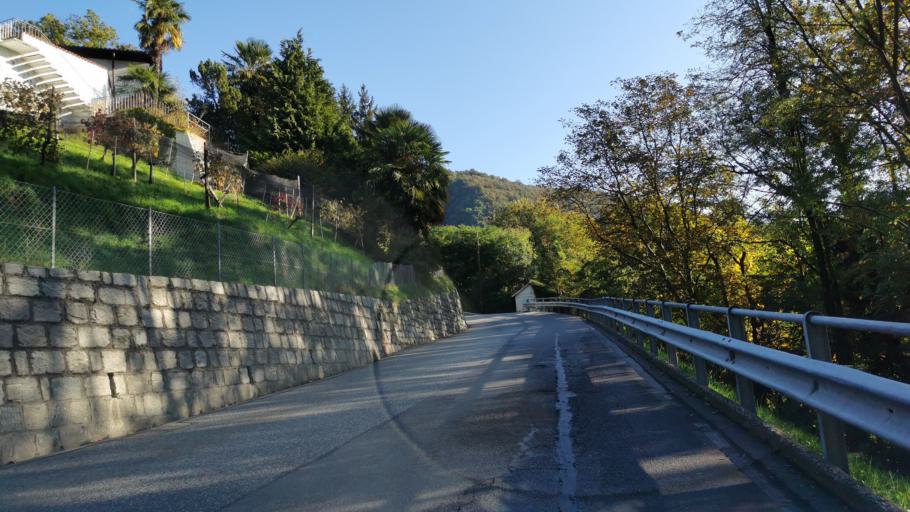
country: CH
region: Ticino
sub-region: Lugano District
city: Pura
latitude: 45.9899
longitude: 8.8664
